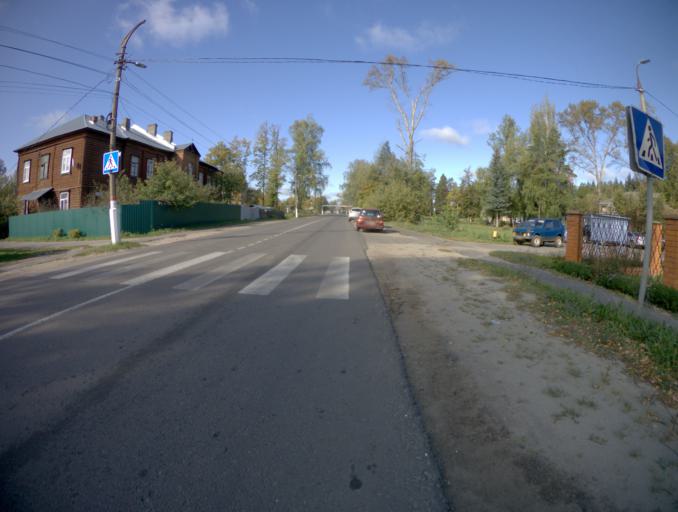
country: RU
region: Moskovskaya
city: Roshal'
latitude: 55.6601
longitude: 39.8810
